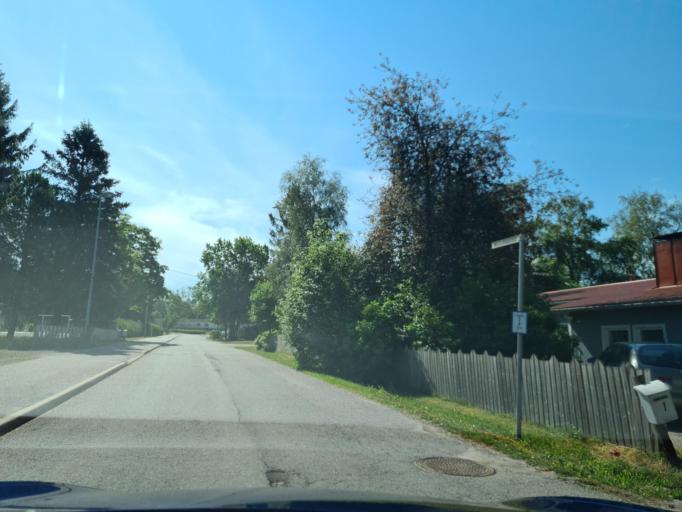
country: FI
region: Varsinais-Suomi
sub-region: Turku
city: Paimio
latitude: 60.4555
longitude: 22.6885
